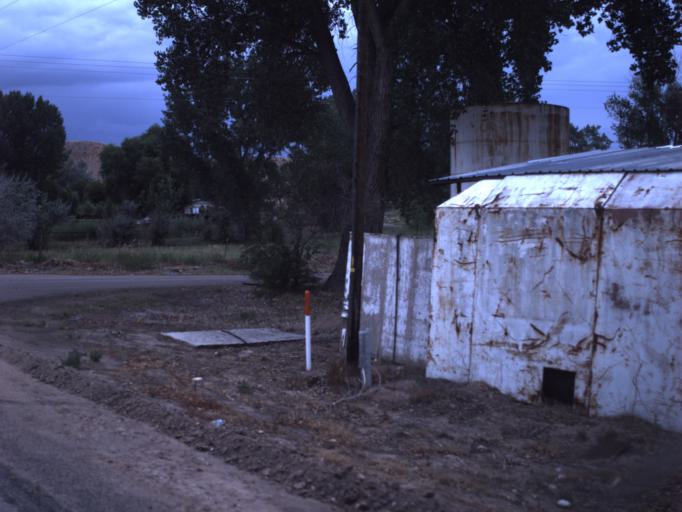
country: US
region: Utah
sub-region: Duchesne County
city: Roosevelt
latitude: 40.3163
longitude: -110.0132
